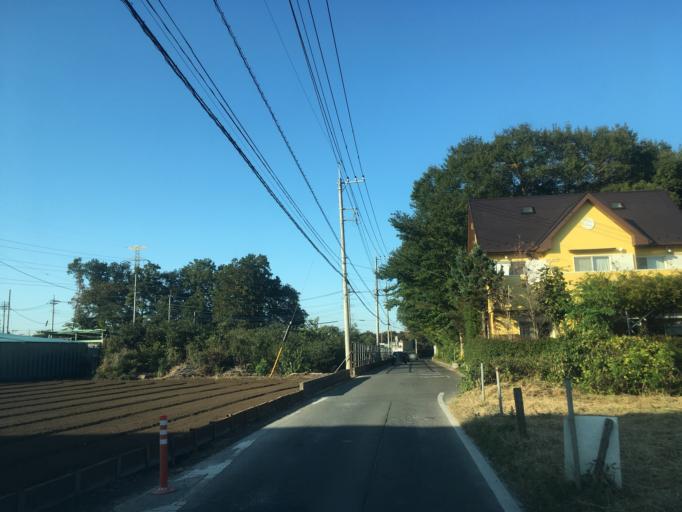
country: JP
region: Saitama
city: Tokorozawa
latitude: 35.8143
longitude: 139.4397
